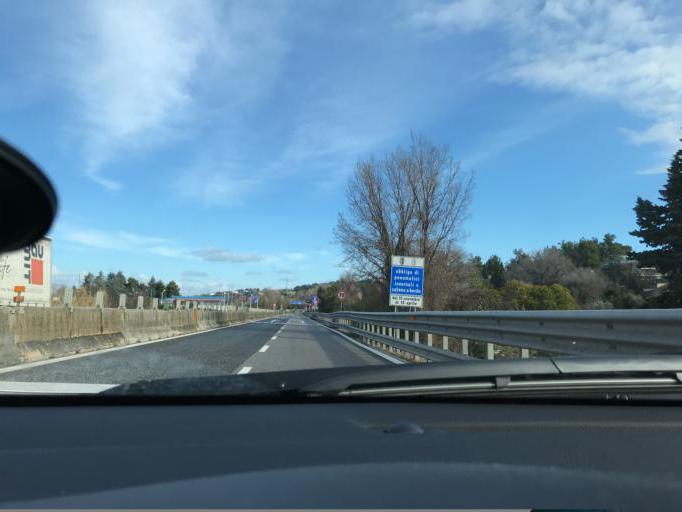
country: IT
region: The Marches
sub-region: Provincia di Ancona
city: Falconara Marittima
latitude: 43.6117
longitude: 13.3769
